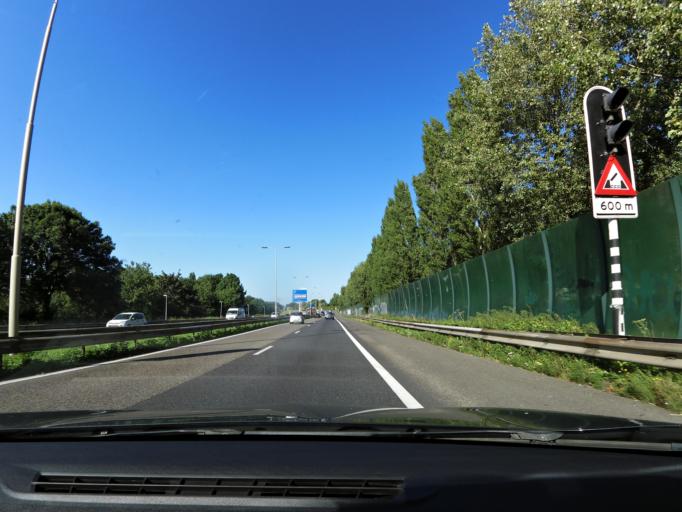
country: NL
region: South Holland
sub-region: Gemeente Papendrecht
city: Papendrecht
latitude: 51.8086
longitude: 4.7033
